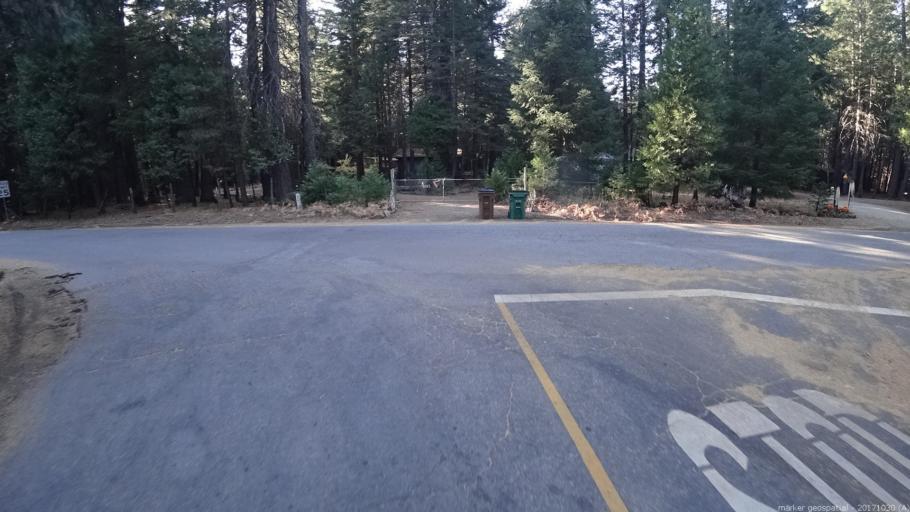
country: US
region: California
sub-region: Shasta County
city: Shingletown
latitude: 40.5586
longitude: -121.7259
